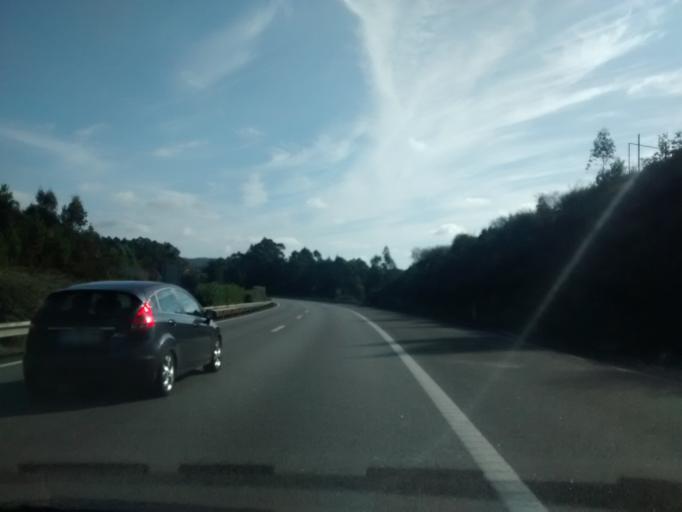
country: PT
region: Porto
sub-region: Santo Tirso
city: Santo Tirso
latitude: 41.3545
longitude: -8.5063
